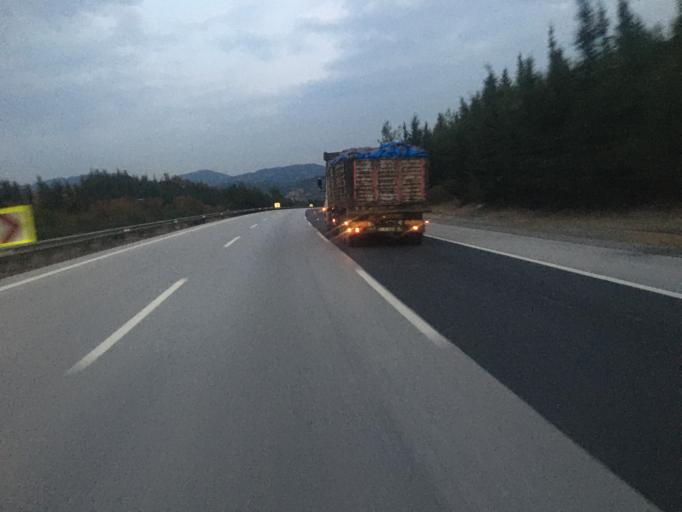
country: TR
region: Osmaniye
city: Haruniye
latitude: 37.2007
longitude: 36.3917
